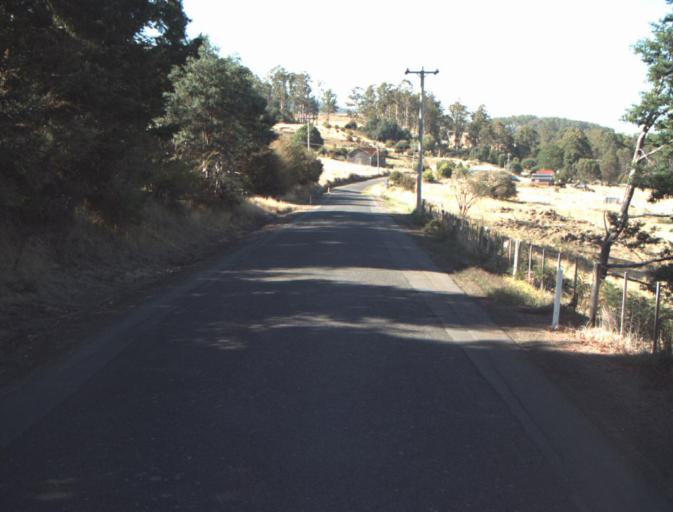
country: AU
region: Tasmania
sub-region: Launceston
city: Newstead
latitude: -41.3505
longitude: 147.3034
